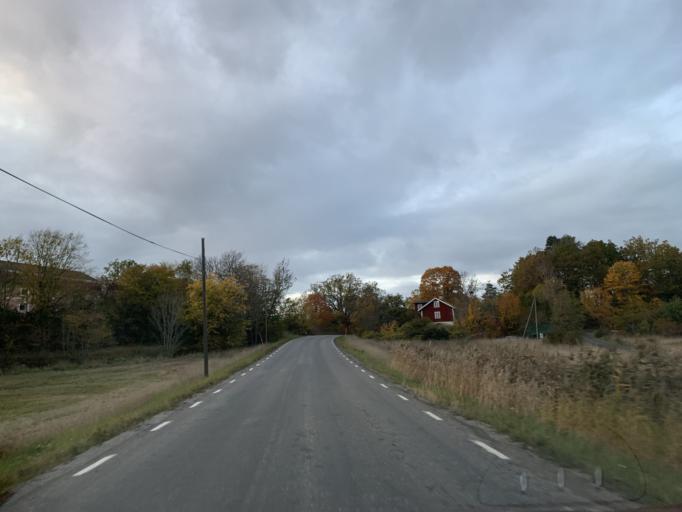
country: SE
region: Stockholm
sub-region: Nynashamns Kommun
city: Osmo
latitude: 58.9269
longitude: 17.7712
